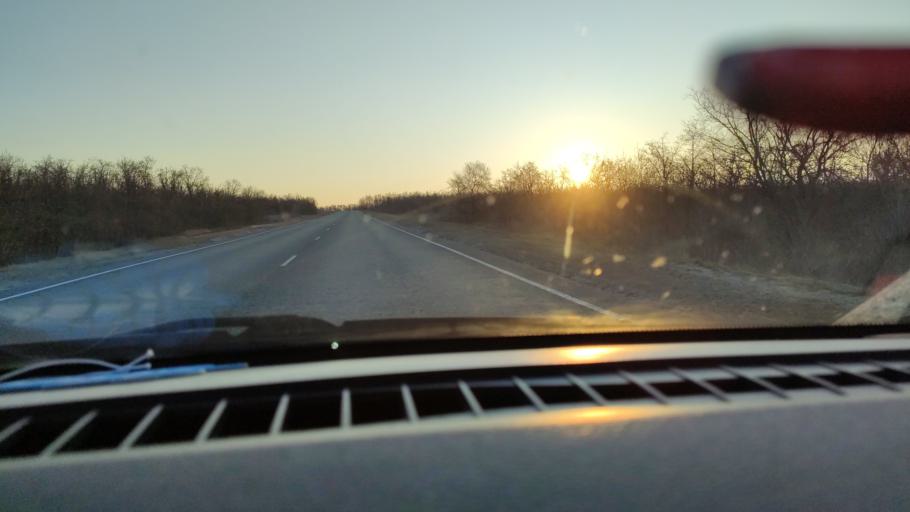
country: RU
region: Saratov
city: Sinodskoye
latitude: 51.9330
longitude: 46.5844
